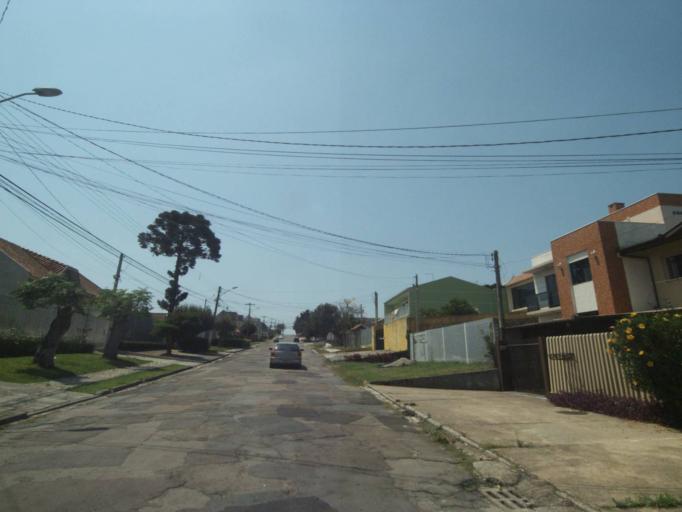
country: BR
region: Parana
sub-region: Sao Jose Dos Pinhais
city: Sao Jose dos Pinhais
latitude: -25.5173
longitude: -49.2649
